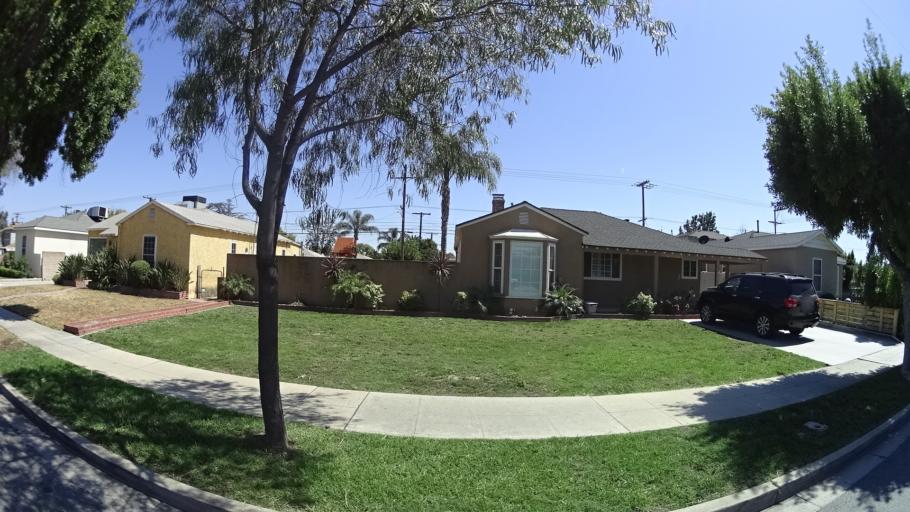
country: US
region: California
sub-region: Los Angeles County
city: North Hollywood
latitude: 34.1849
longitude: -118.3571
